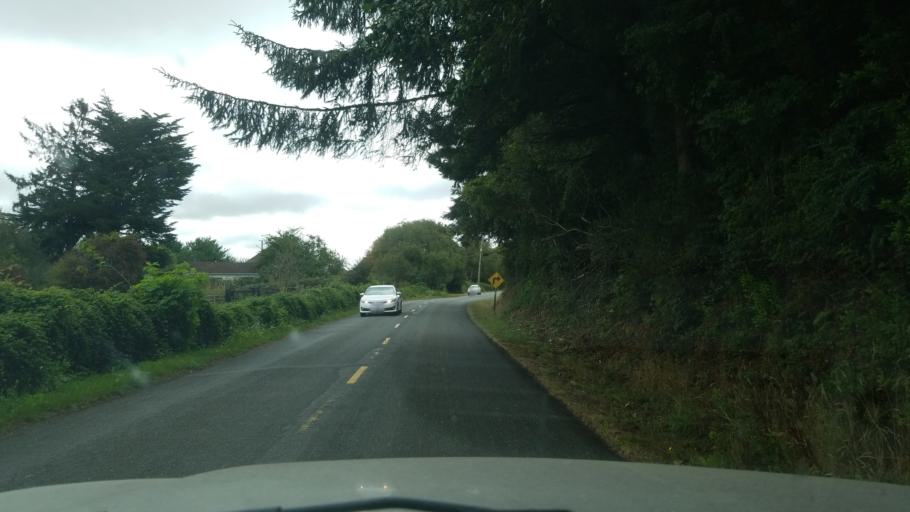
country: US
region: California
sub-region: Humboldt County
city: Ferndale
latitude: 40.5793
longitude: -124.2712
